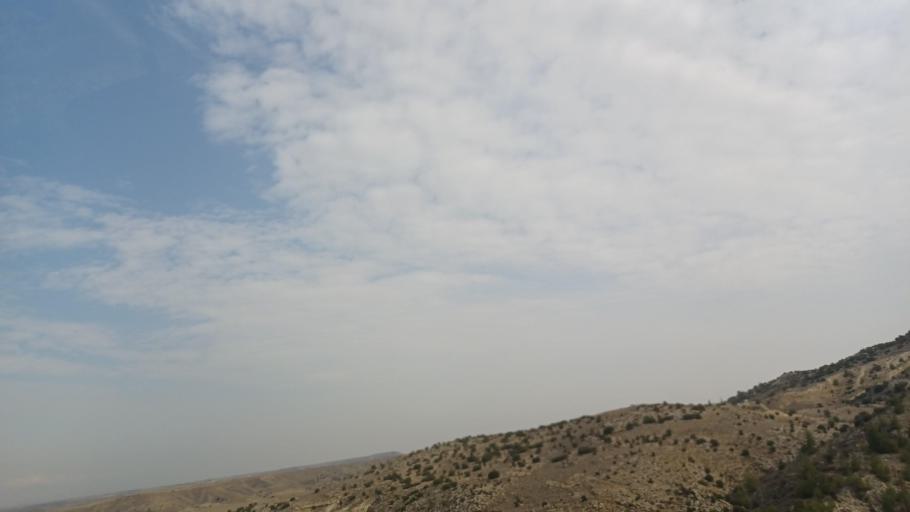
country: CY
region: Lefkosia
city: Meniko
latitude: 35.0555
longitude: 33.1280
